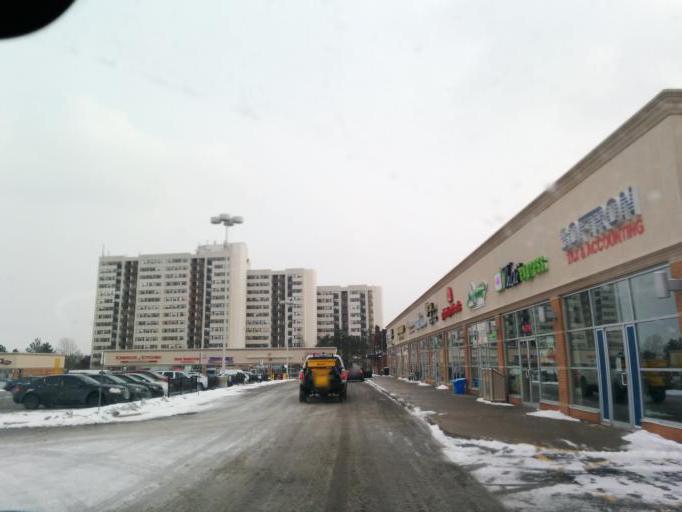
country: CA
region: Ontario
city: Mississauga
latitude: 43.5806
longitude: -79.7596
